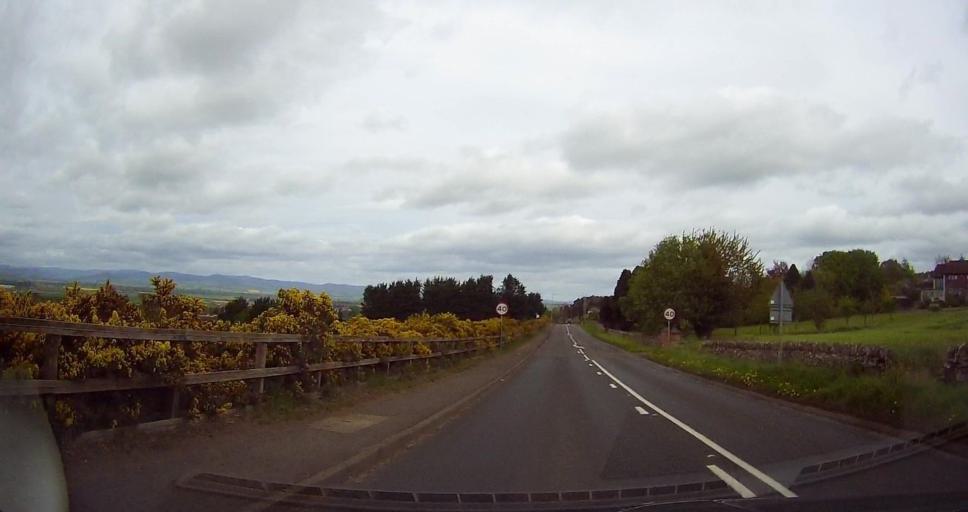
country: GB
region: Scotland
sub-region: Angus
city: Forfar
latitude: 56.6259
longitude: -2.8999
